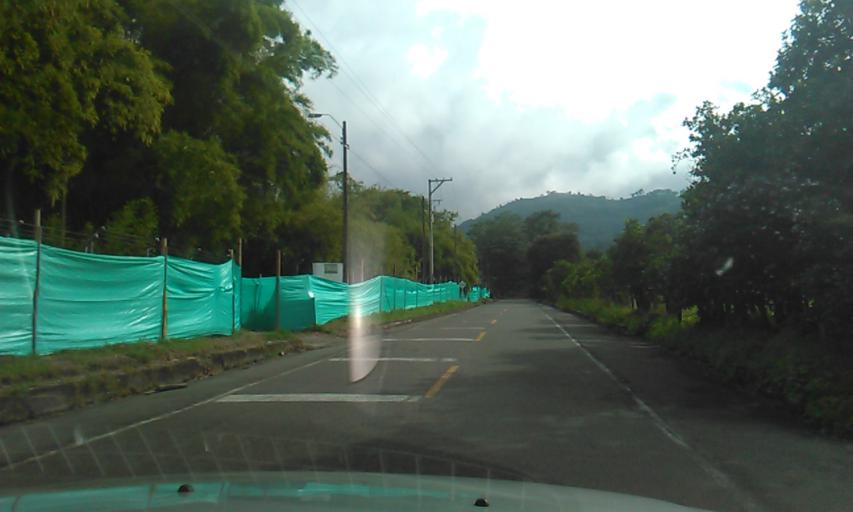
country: CO
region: Quindio
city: Cordoba
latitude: 4.4020
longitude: -75.7153
